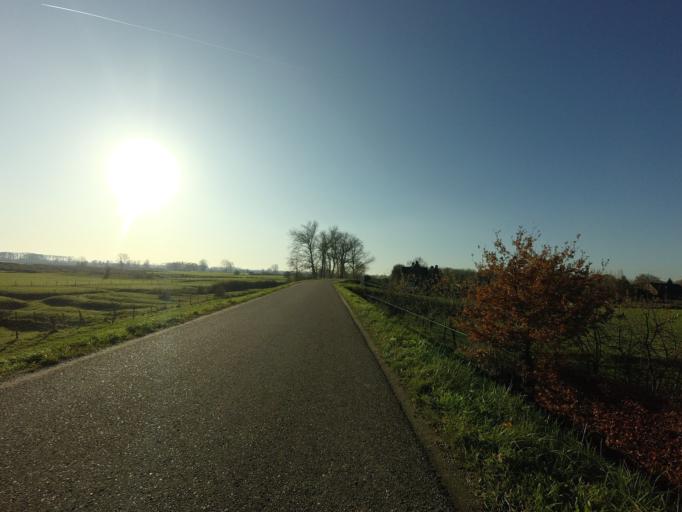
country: NL
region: North Brabant
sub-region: Gemeente 's-Hertogenbosch
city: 's-Hertogenbosch
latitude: 51.7557
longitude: 5.3374
